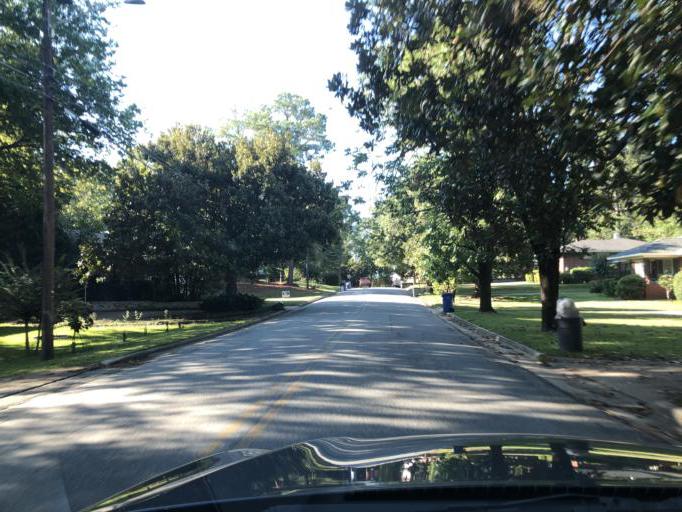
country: US
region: Georgia
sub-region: Muscogee County
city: Columbus
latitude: 32.4801
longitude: -84.9475
